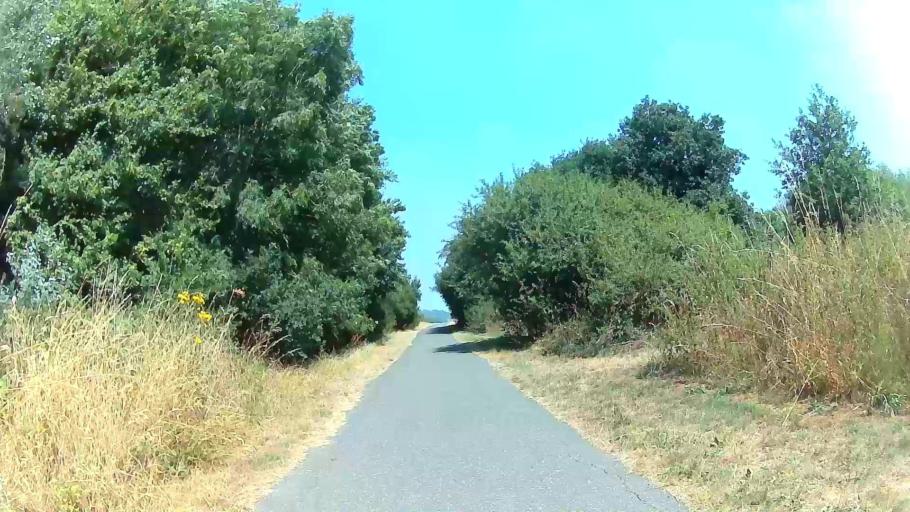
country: GB
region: England
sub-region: Greater London
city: Elm Park
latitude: 51.5336
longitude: 0.2117
